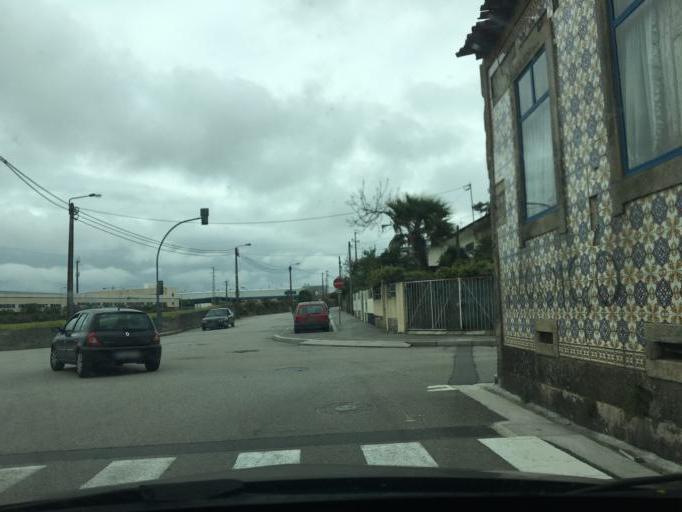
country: PT
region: Porto
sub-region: Matosinhos
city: Santa Cruz do Bispo
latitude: 41.2323
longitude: -8.6611
